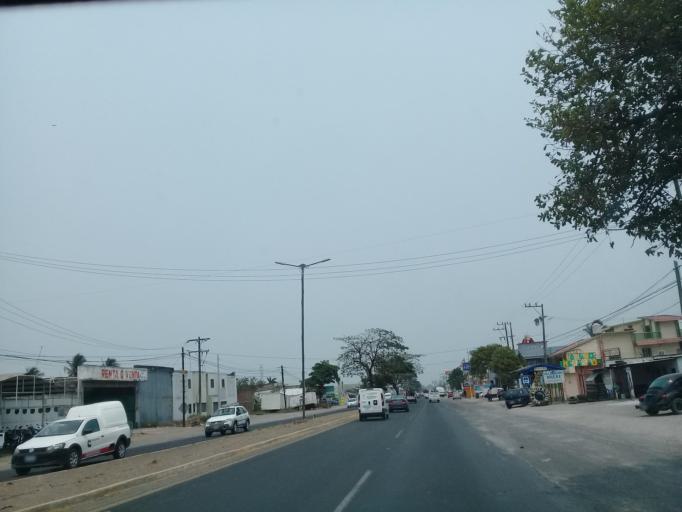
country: MX
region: Veracruz
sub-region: Veracruz
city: Las Amapolas
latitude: 19.1635
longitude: -96.2104
